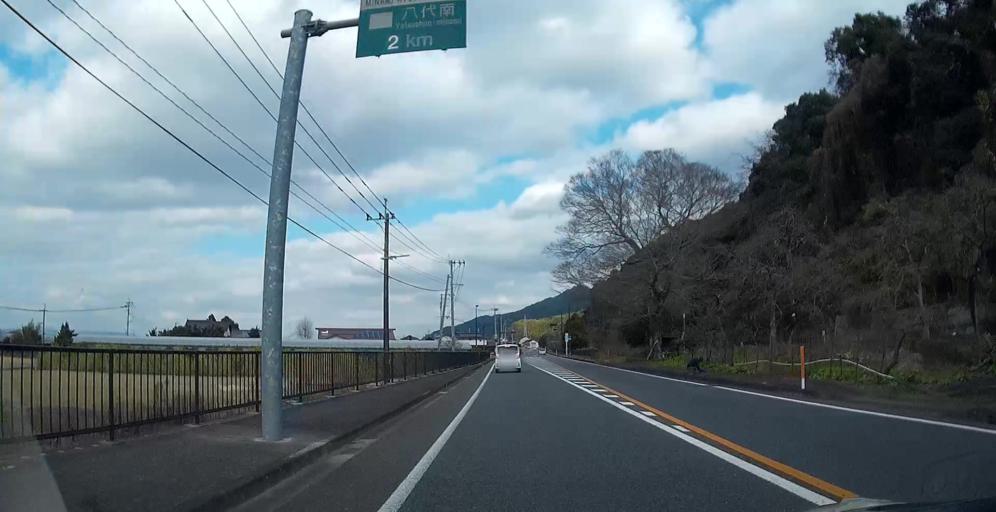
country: JP
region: Kumamoto
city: Yatsushiro
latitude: 32.4479
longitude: 130.5886
